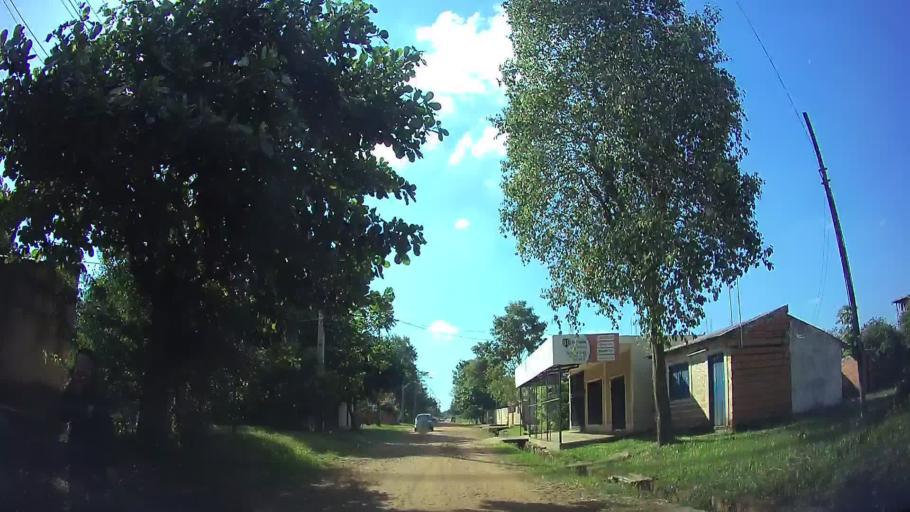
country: PY
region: Central
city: Limpio
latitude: -25.2451
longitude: -57.4743
